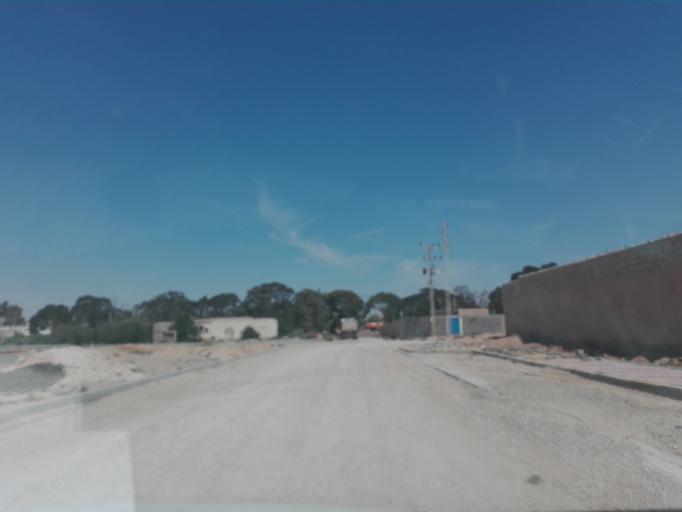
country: TN
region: Safaqis
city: Sfax
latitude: 34.7286
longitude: 10.5194
